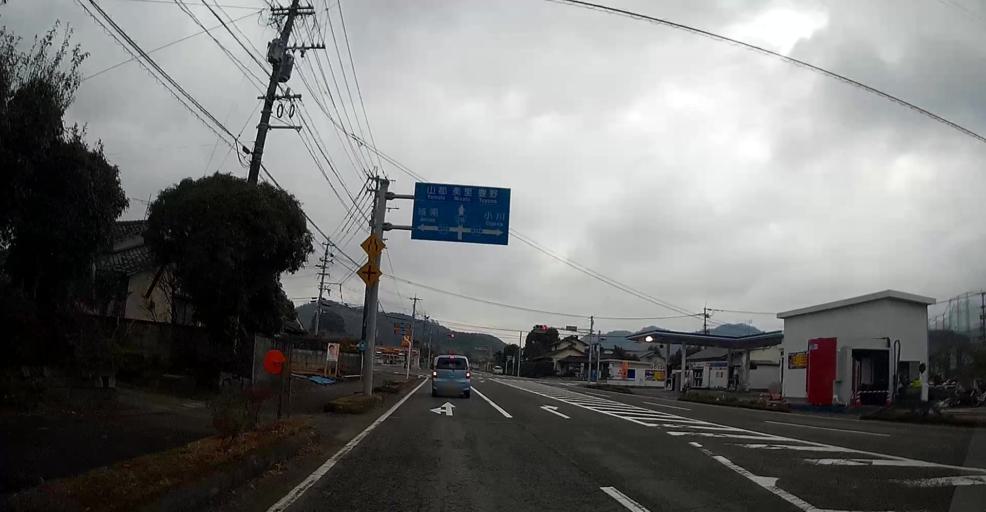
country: JP
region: Kumamoto
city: Matsubase
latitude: 32.6494
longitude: 130.7152
